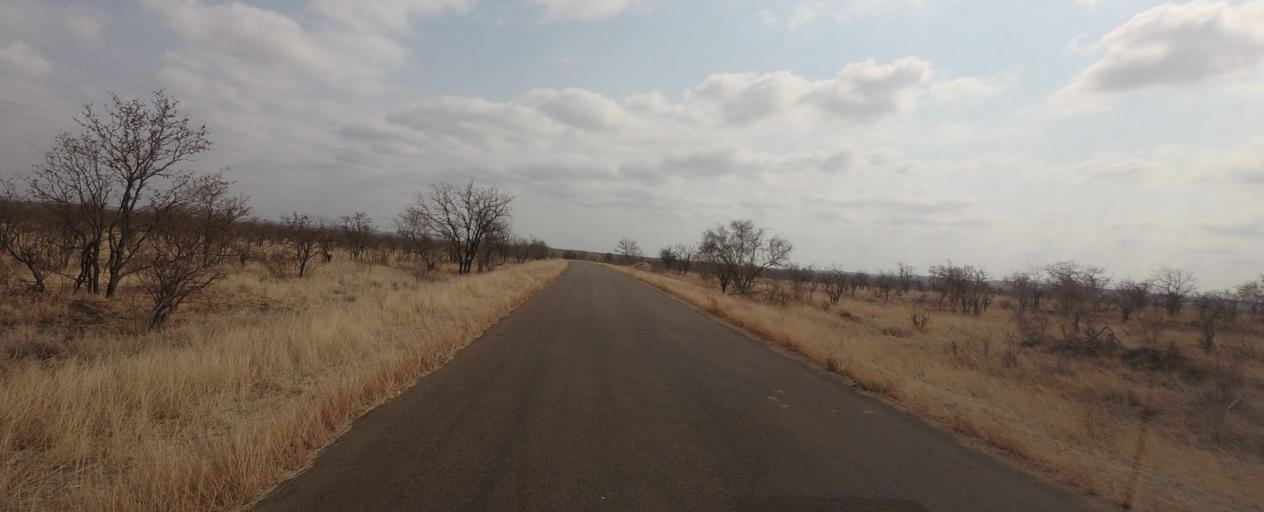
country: ZA
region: Limpopo
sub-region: Vhembe District Municipality
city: Mutale
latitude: -22.5680
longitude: 31.1917
